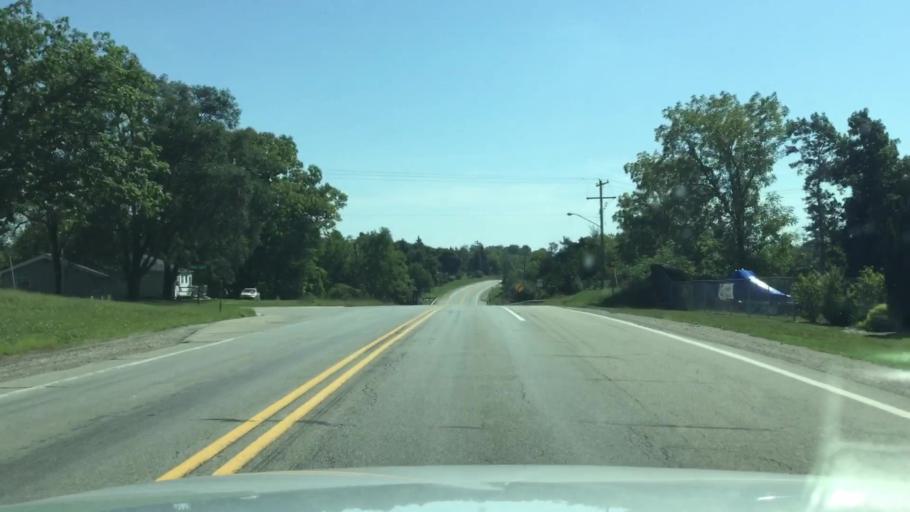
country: US
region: Michigan
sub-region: Lenawee County
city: Manitou Beach-Devils Lake
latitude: 42.0030
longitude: -84.2766
